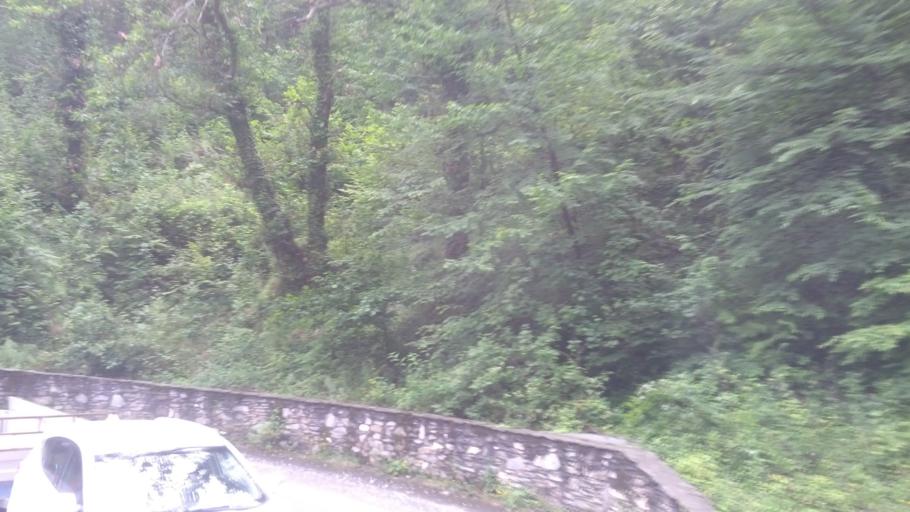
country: IT
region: Tuscany
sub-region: Provincia di Massa-Carrara
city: Massa
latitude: 44.0775
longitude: 10.1340
